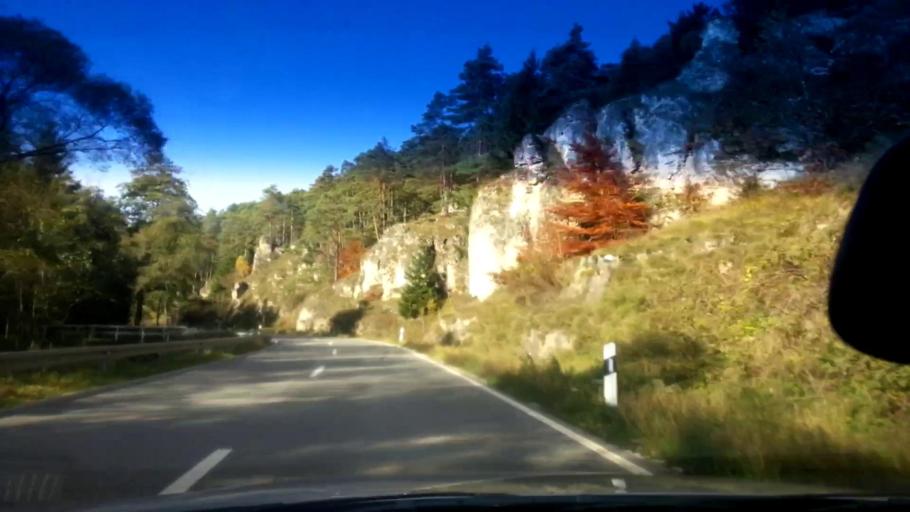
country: DE
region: Bavaria
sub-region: Upper Franconia
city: Stadelhofen
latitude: 49.9688
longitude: 11.1945
